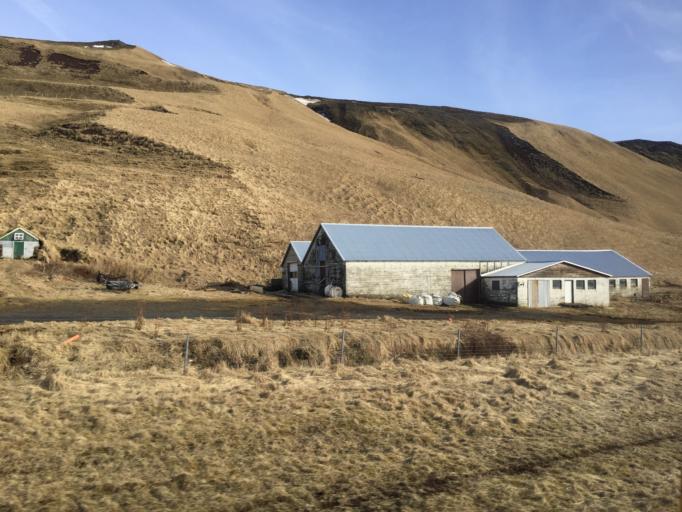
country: IS
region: South
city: Vestmannaeyjar
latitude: 63.4154
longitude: -19.0480
